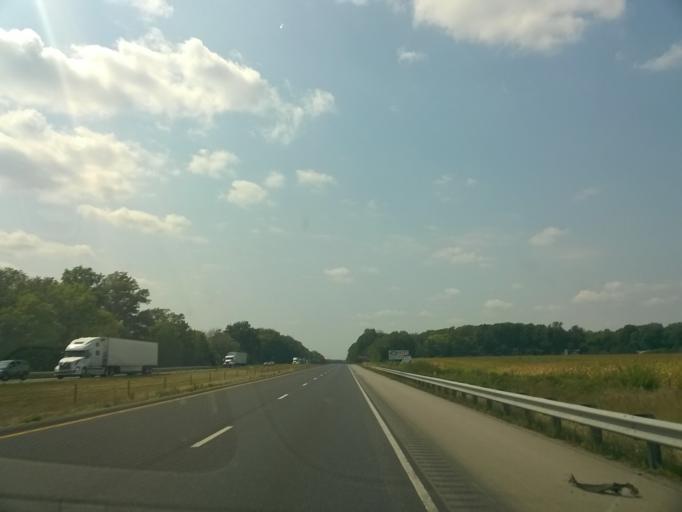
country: US
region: Indiana
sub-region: Vigo County
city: Terre Haute
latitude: 39.4309
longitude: -87.3654
